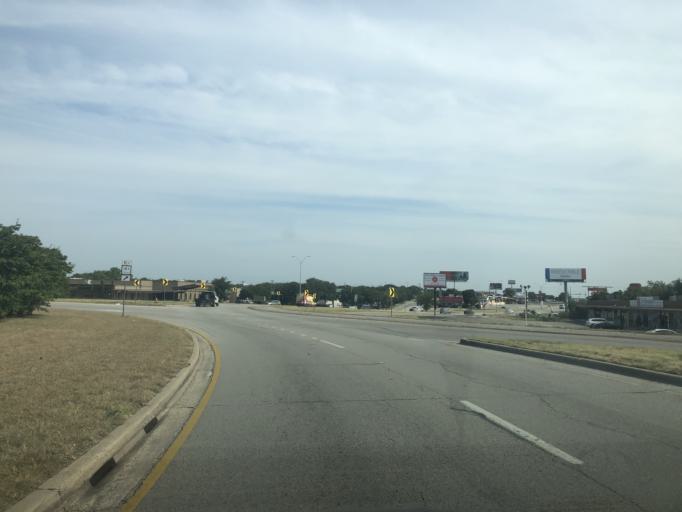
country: US
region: Texas
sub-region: Tarrant County
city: White Settlement
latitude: 32.7178
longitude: -97.4420
